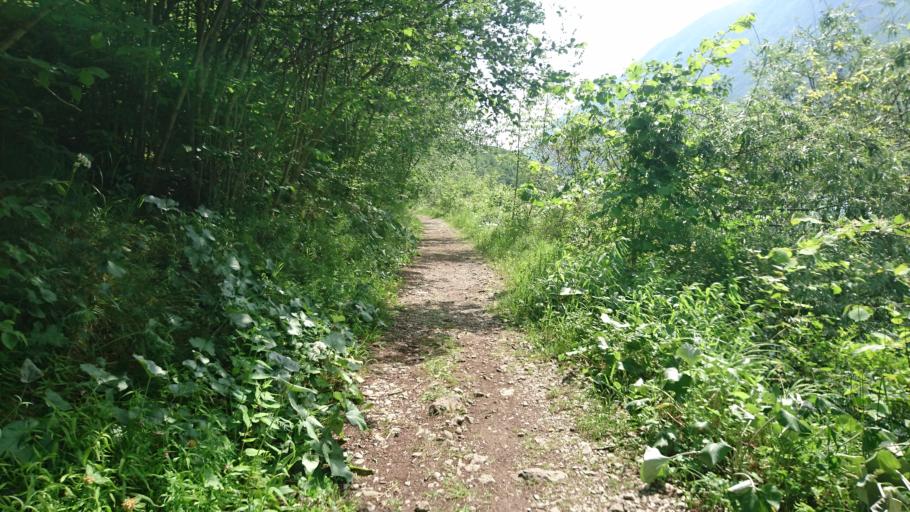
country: IT
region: Veneto
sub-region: Provincia di Treviso
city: Fregona
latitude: 46.0593
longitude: 12.3250
